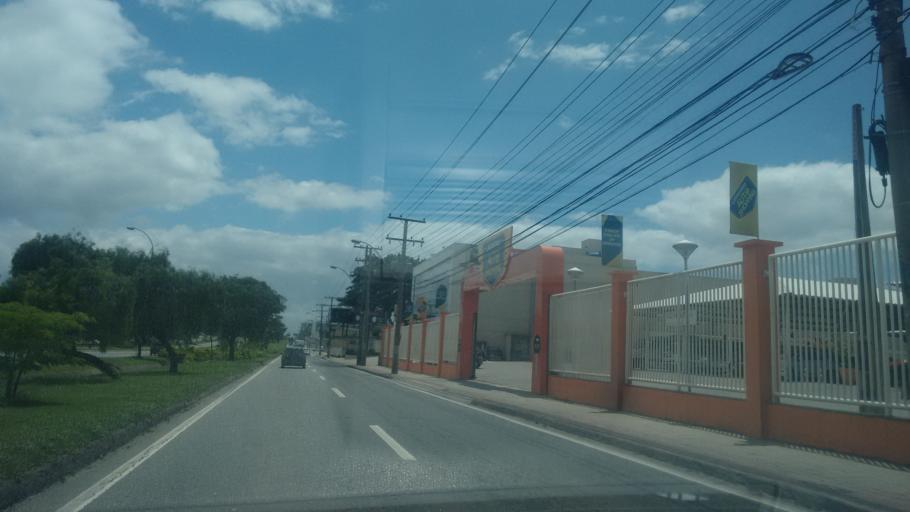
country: BR
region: Espirito Santo
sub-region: Serra
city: Serra
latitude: -20.2015
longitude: -40.2689
